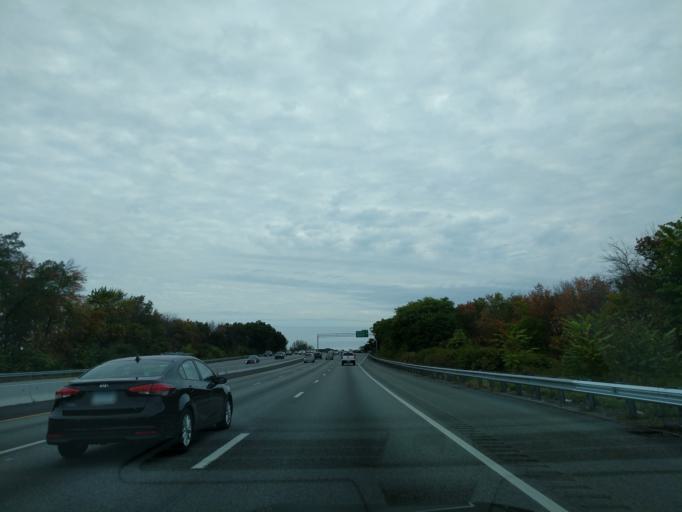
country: US
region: Massachusetts
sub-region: Middlesex County
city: Reading
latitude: 42.5123
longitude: -71.0915
